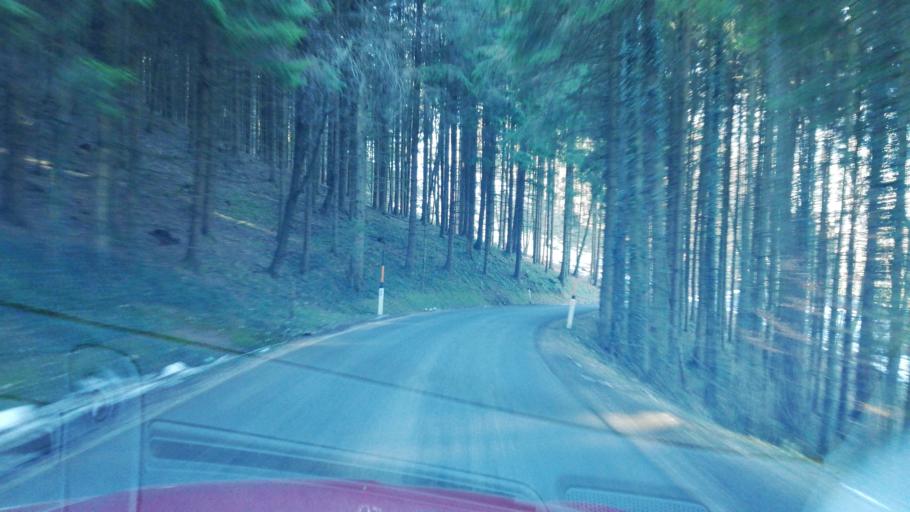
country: AT
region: Upper Austria
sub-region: Politischer Bezirk Vocklabruck
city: Vocklabruck
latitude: 47.9858
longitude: 13.6559
